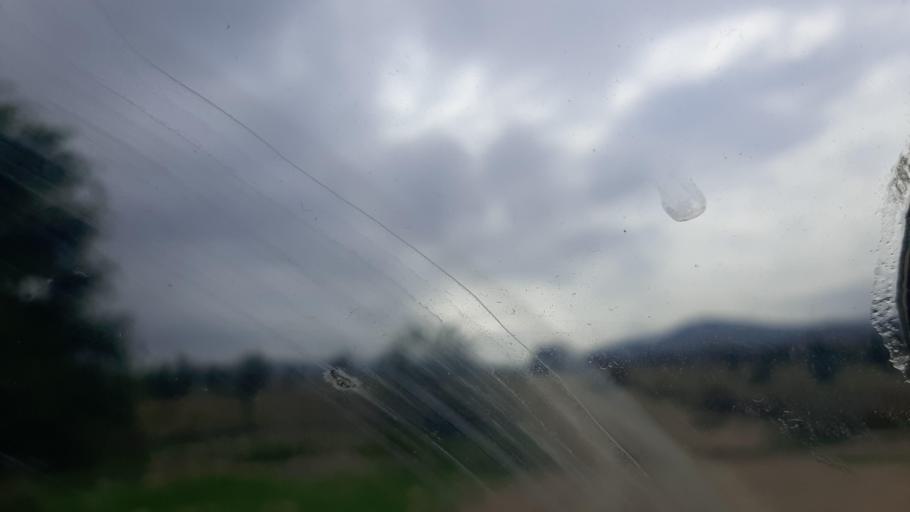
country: TN
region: Tunis
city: La Sebala du Mornag
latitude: 36.5648
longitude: 10.2939
